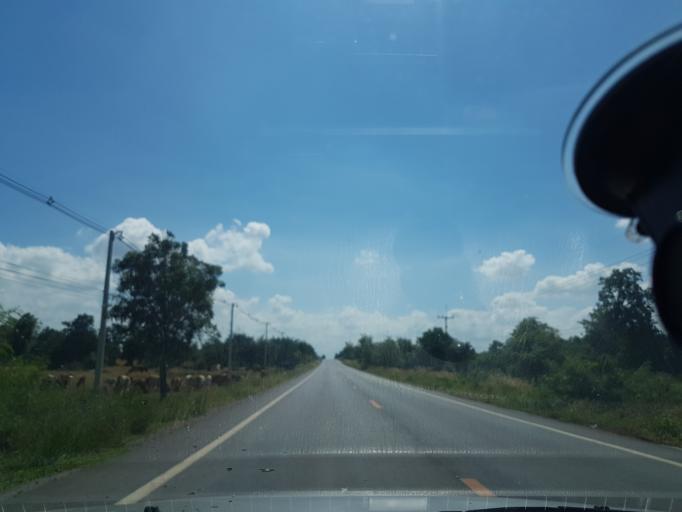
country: TH
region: Lop Buri
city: Phatthana Nikhom
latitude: 14.9512
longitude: 101.0086
